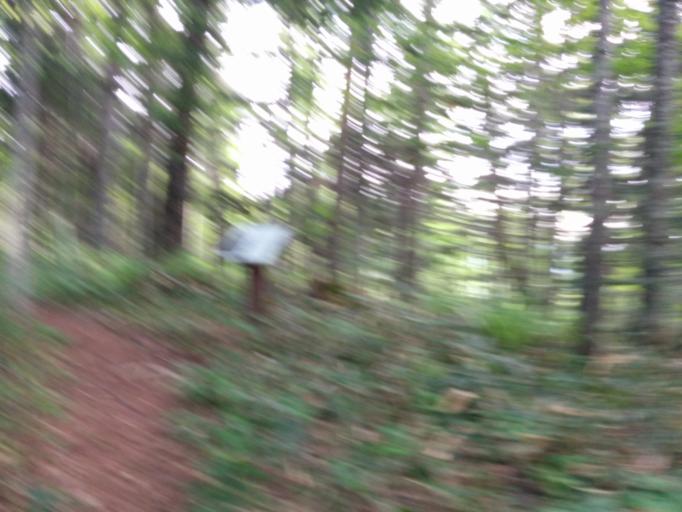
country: JP
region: Hokkaido
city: Bihoro
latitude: 43.4361
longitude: 144.1026
